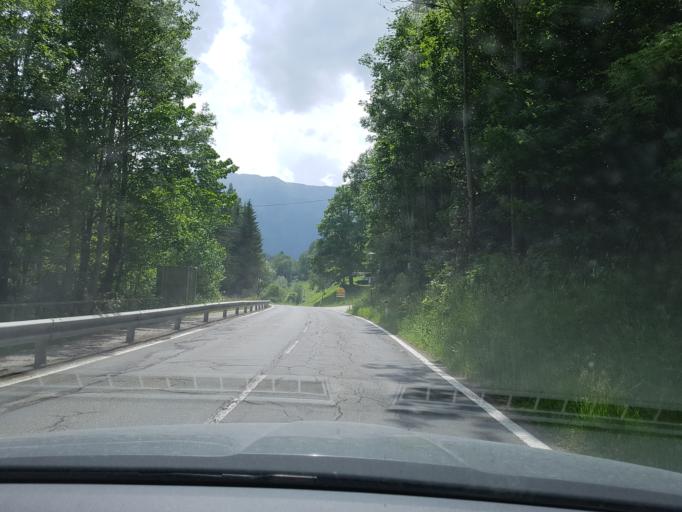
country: AT
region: Carinthia
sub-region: Politischer Bezirk Spittal an der Drau
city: Kleinkirchheim
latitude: 46.8090
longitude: 13.7642
